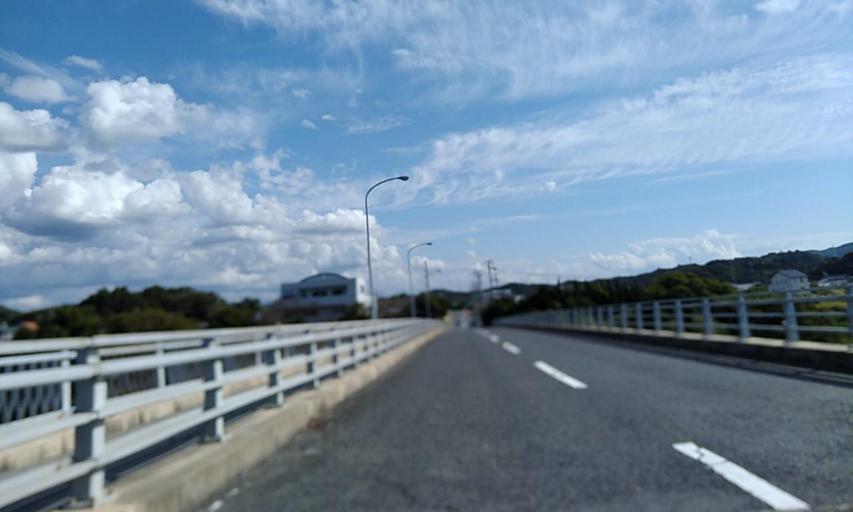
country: JP
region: Wakayama
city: Gobo
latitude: 33.8909
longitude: 135.1687
